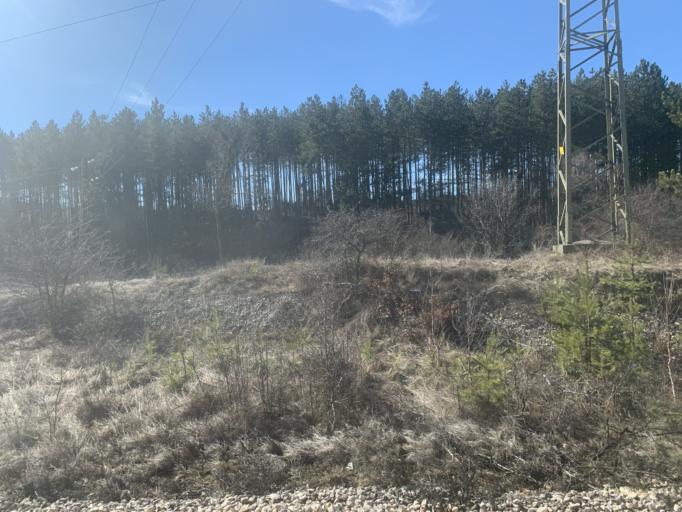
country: BG
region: Sofiya
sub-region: Obshtina Gorna Malina
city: Gorna Malina
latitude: 42.5624
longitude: 23.6915
